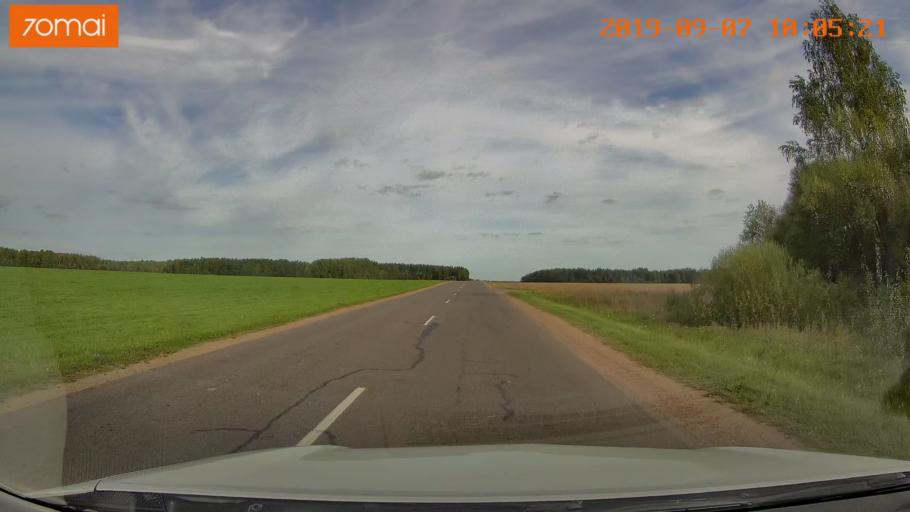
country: BY
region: Grodnenskaya
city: Voranava
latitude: 54.0460
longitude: 25.4079
